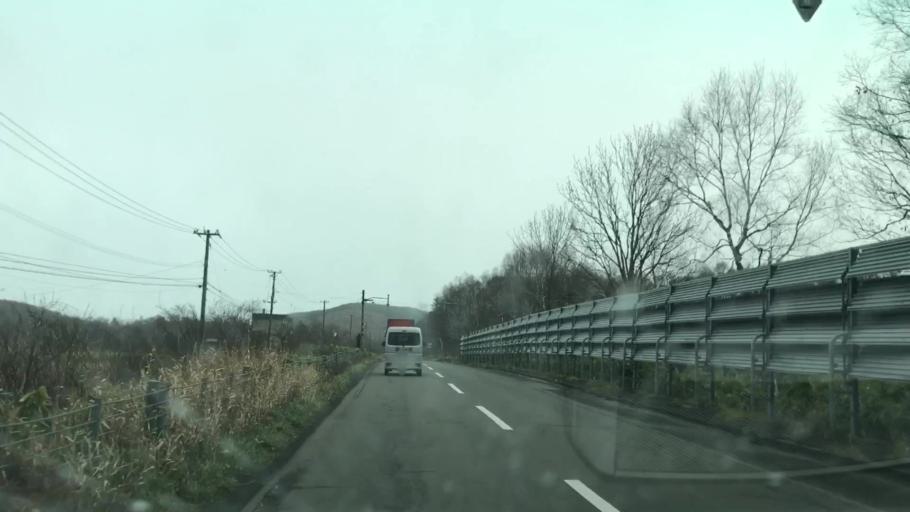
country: JP
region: Hokkaido
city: Yoichi
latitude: 43.3166
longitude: 140.5341
